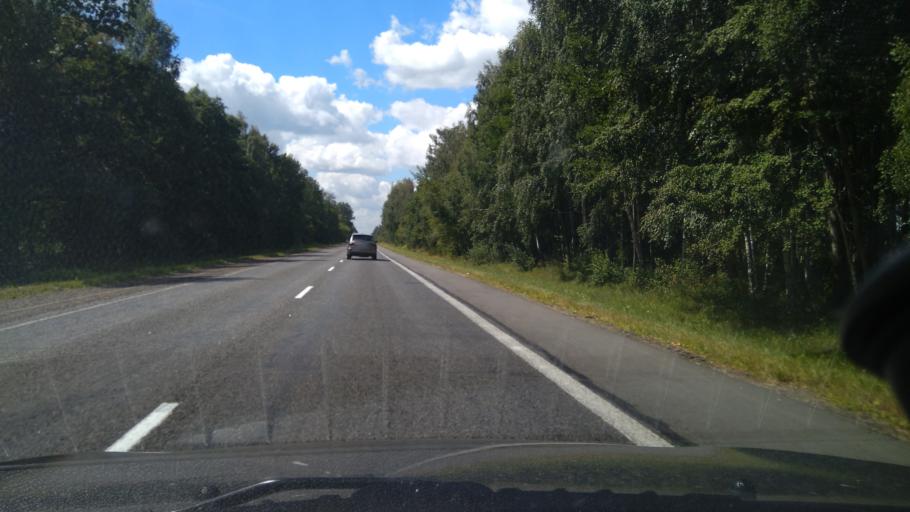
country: BY
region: Brest
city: Ivatsevichy
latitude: 52.6782
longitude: 25.2748
